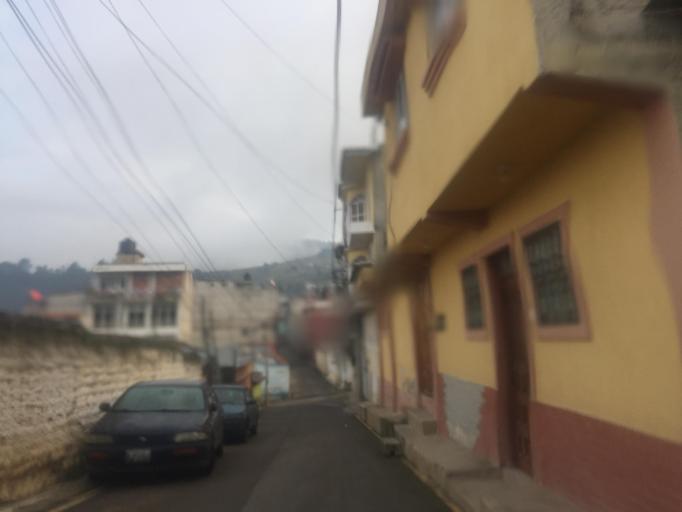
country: GT
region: Totonicapan
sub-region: Municipio de Totonicapan
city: Totonicapan
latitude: 14.9138
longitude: -91.3564
